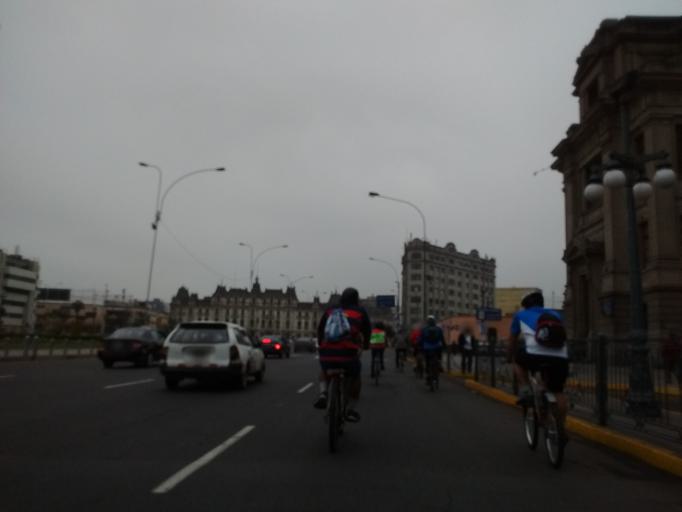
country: PE
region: Lima
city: Lima
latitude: -12.0575
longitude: -77.0355
